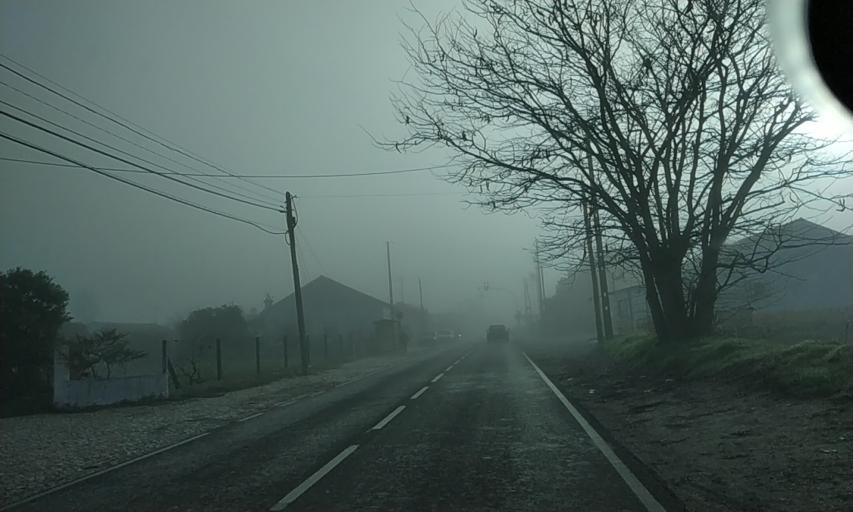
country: PT
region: Setubal
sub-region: Palmela
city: Pinhal Novo
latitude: 38.6145
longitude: -8.8845
